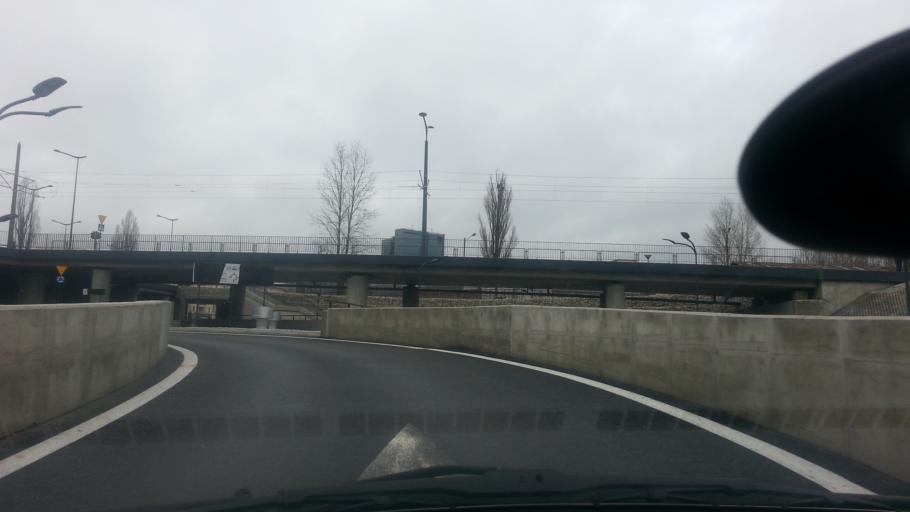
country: PL
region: Lodz Voivodeship
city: Lodz
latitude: 51.7693
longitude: 19.4737
